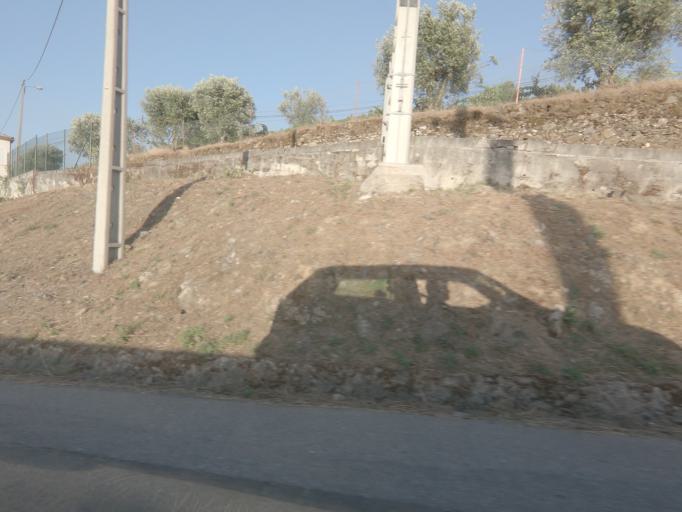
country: PT
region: Viseu
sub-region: Armamar
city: Armamar
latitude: 41.1892
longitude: -7.6886
